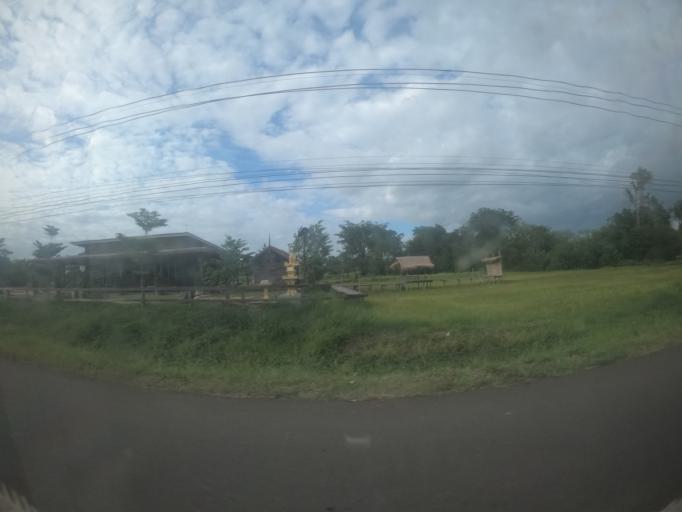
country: TH
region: Surin
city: Prasat
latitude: 14.5926
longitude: 103.4476
